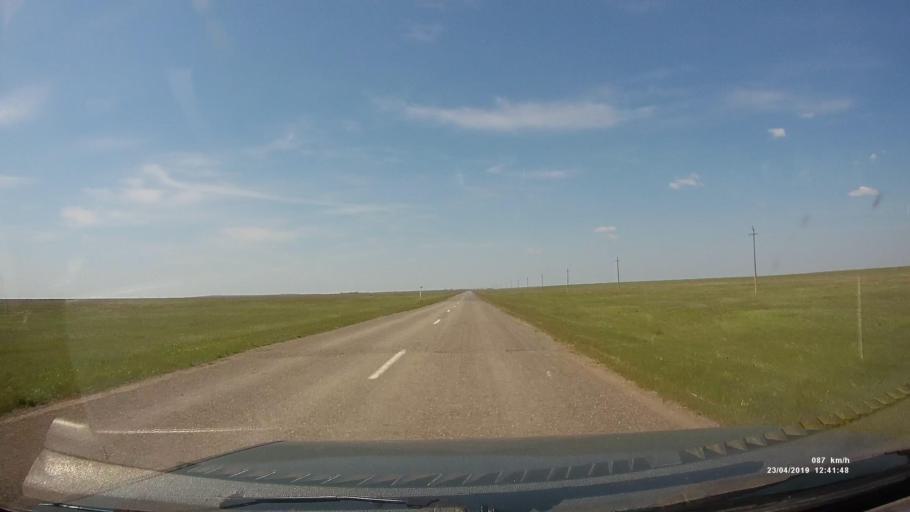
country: RU
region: Kalmykiya
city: Yashalta
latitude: 46.4510
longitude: 42.6754
